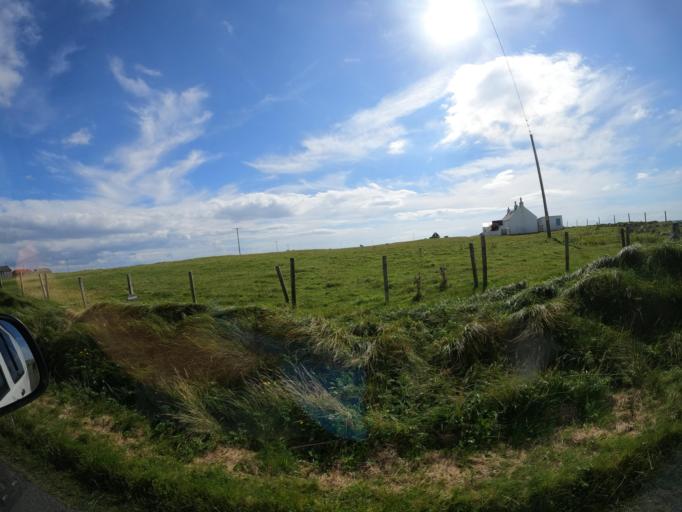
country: GB
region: Scotland
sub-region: Eilean Siar
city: Barra
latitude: 56.4938
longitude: -6.8190
